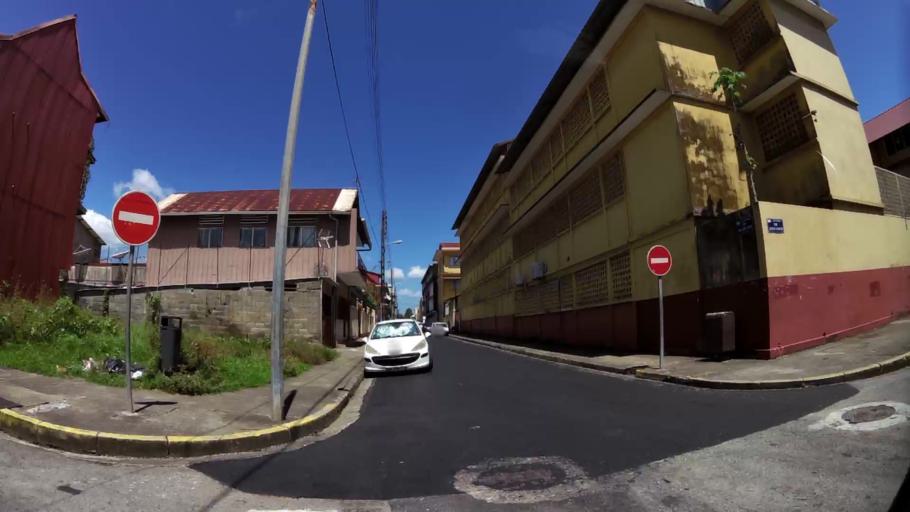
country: GF
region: Guyane
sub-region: Guyane
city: Cayenne
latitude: 4.9410
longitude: -52.3310
